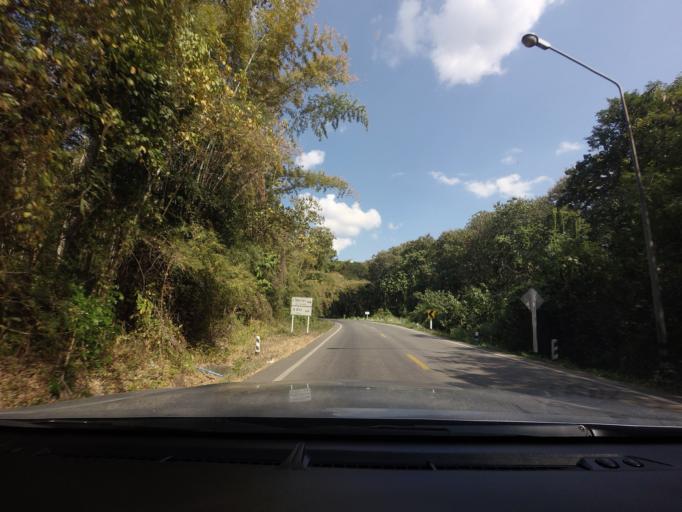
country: TH
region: Chiang Mai
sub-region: Amphoe Chiang Dao
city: Chiang Dao
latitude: 19.4603
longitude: 98.9951
